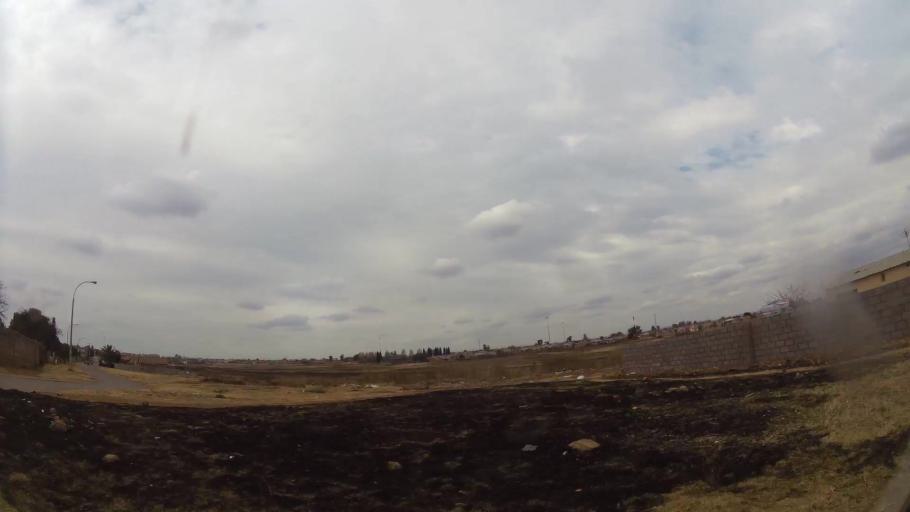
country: ZA
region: Gauteng
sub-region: Ekurhuleni Metropolitan Municipality
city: Germiston
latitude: -26.3875
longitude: 28.1224
